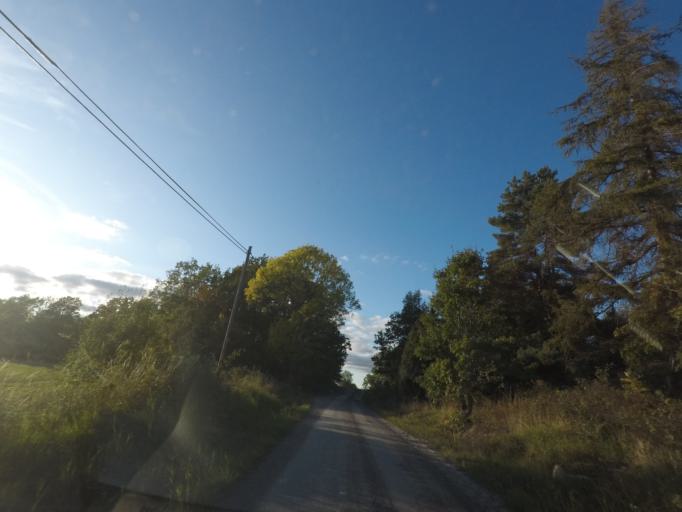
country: SE
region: Vaestmanland
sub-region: Hallstahammars Kommun
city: Kolback
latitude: 59.4821
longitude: 16.1898
